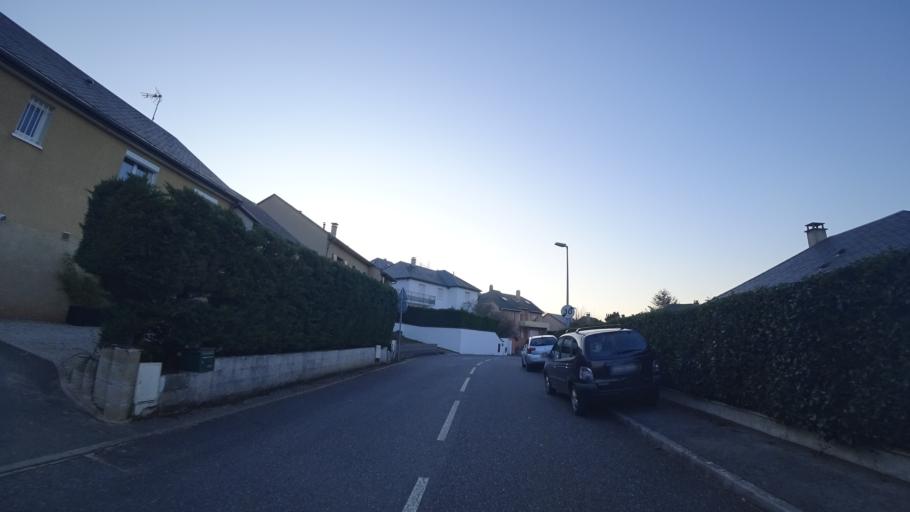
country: FR
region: Midi-Pyrenees
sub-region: Departement de l'Aveyron
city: Rodez
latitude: 44.3644
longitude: 2.5595
